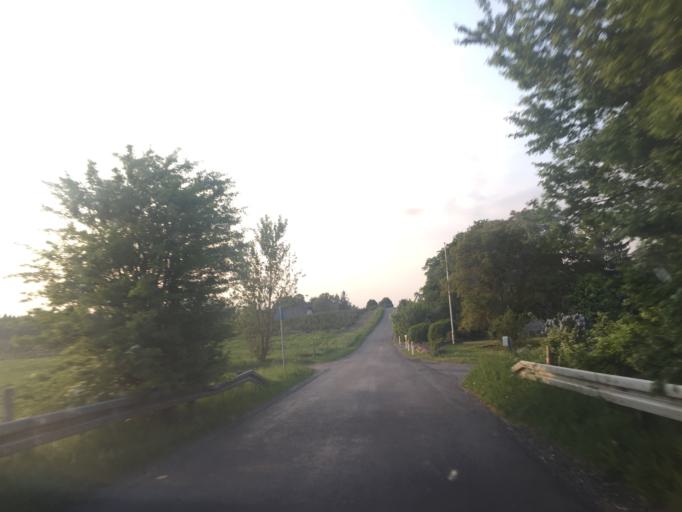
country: DK
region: South Denmark
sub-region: Odense Kommune
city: Bellinge
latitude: 55.3775
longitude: 10.3104
